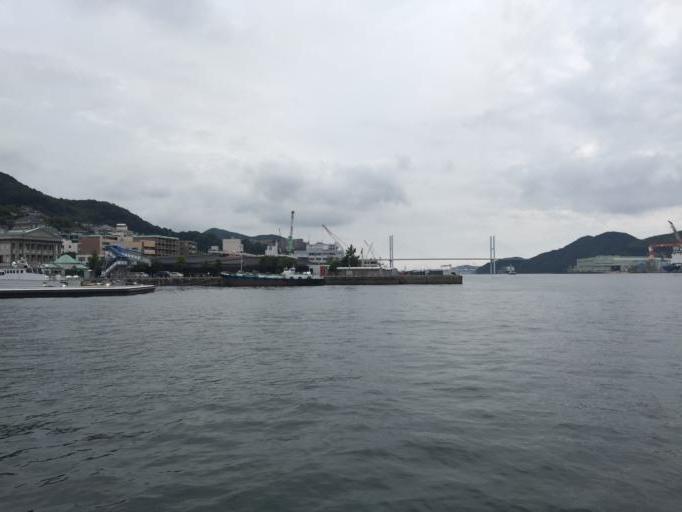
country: JP
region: Nagasaki
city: Nagasaki-shi
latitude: 32.7387
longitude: 129.8695
